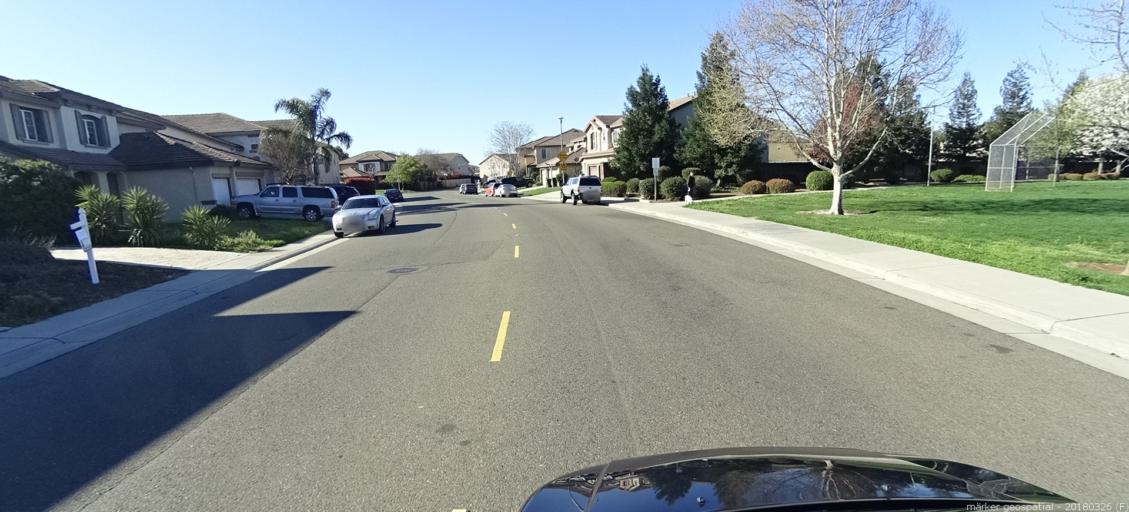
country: US
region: California
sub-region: Sacramento County
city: Vineyard
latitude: 38.4764
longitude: -121.3746
